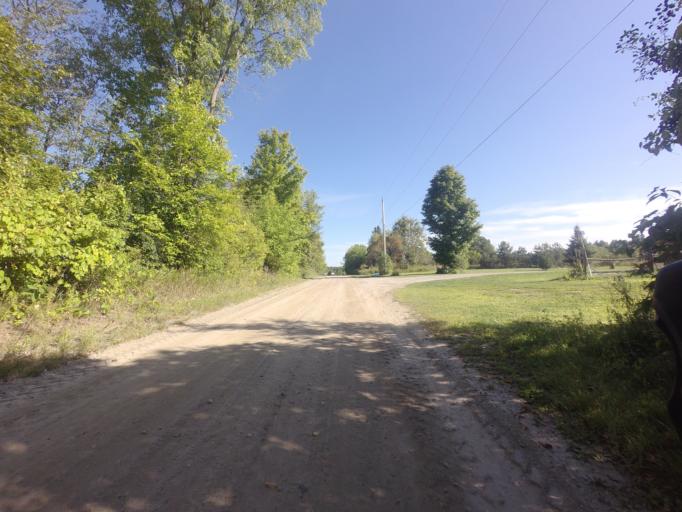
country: CA
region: Ontario
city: Perth
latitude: 44.9372
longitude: -76.3761
